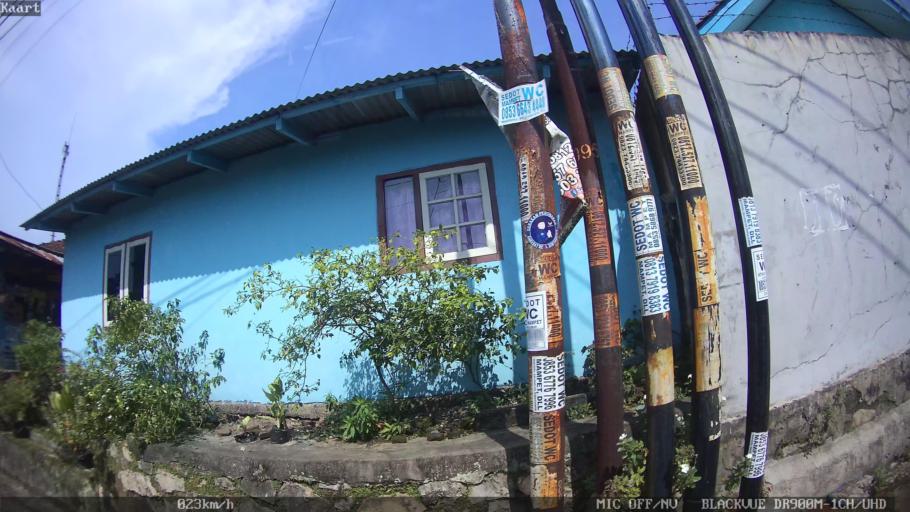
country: ID
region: Lampung
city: Kedaton
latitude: -5.3951
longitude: 105.2371
